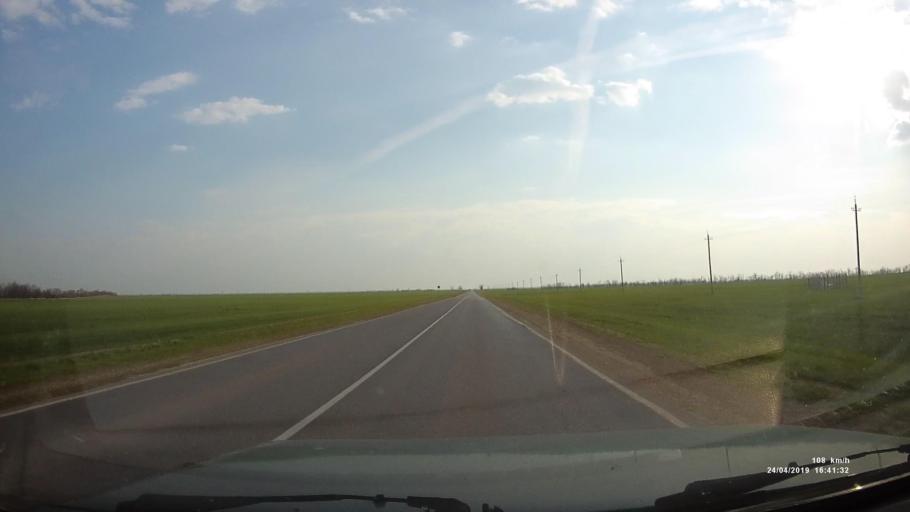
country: RU
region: Rostov
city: Gundorovskiy
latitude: 46.8189
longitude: 41.8662
